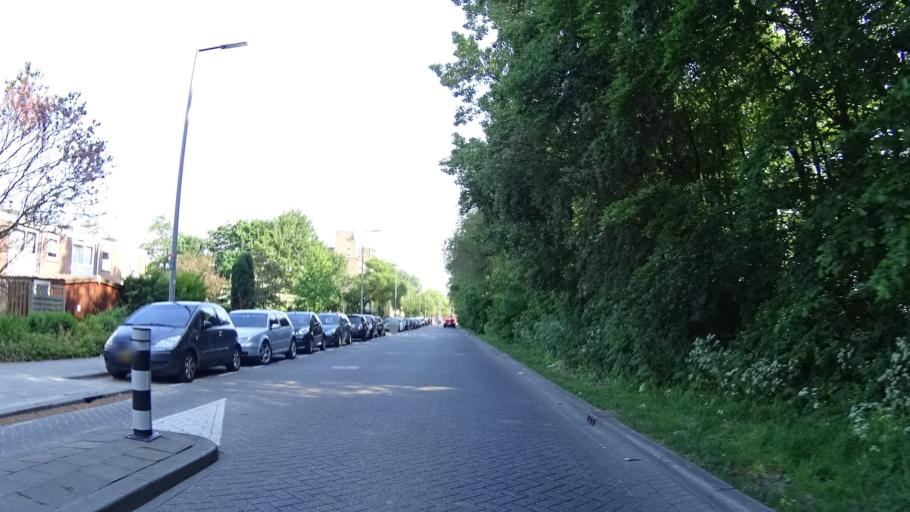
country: NL
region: South Holland
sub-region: Gemeente Barendrecht
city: Barendrecht
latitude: 51.8839
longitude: 4.5309
